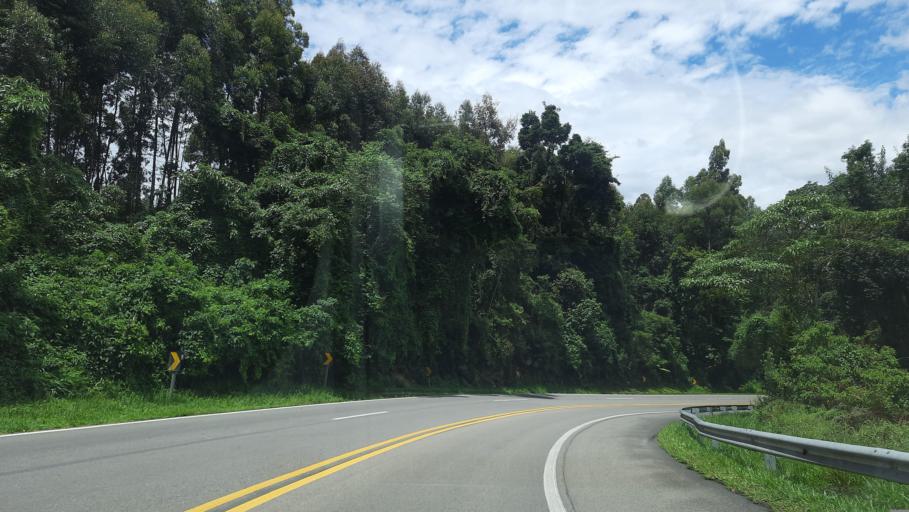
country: BR
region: Minas Gerais
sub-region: Pocos De Caldas
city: Pocos de Caldas
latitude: -21.8438
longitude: -46.6985
